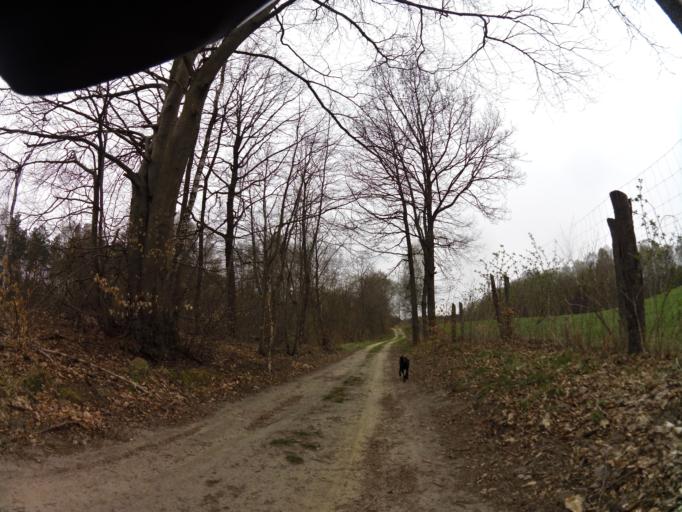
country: PL
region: West Pomeranian Voivodeship
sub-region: Powiat koszalinski
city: Bobolice
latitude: 53.9398
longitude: 16.6944
